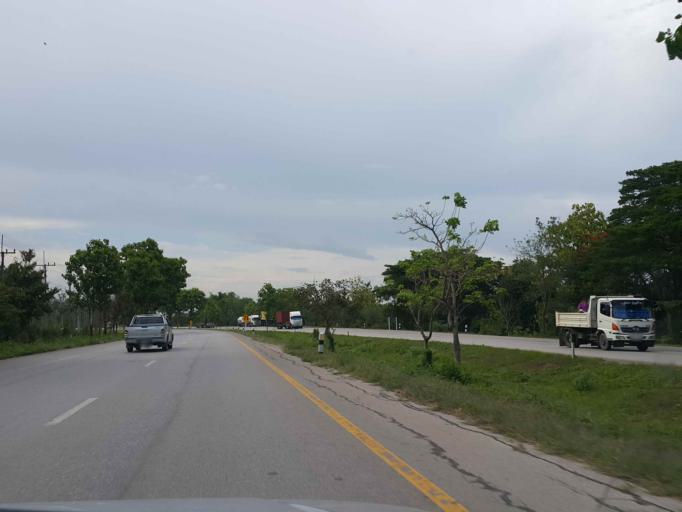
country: TH
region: Lampang
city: Ko Kha
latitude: 18.1779
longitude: 99.4086
